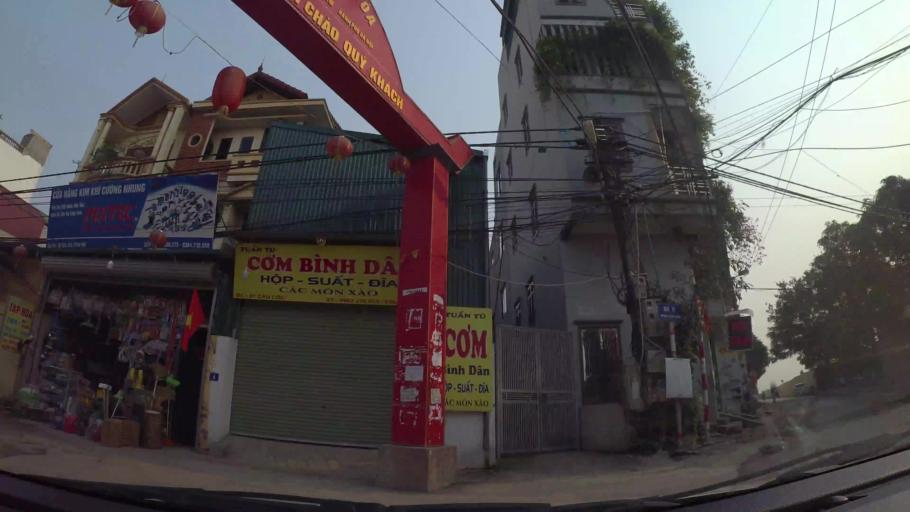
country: VN
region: Ha Noi
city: Cau Dien
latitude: 21.0038
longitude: 105.7423
